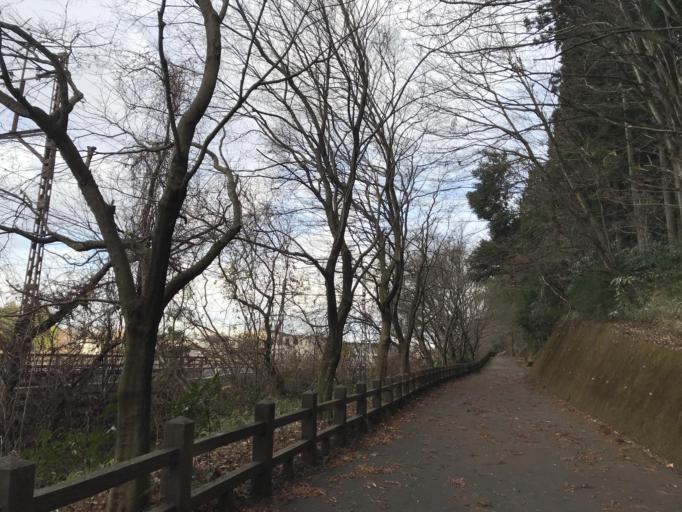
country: JP
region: Tochigi
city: Imaichi
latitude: 36.7290
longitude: 139.6763
